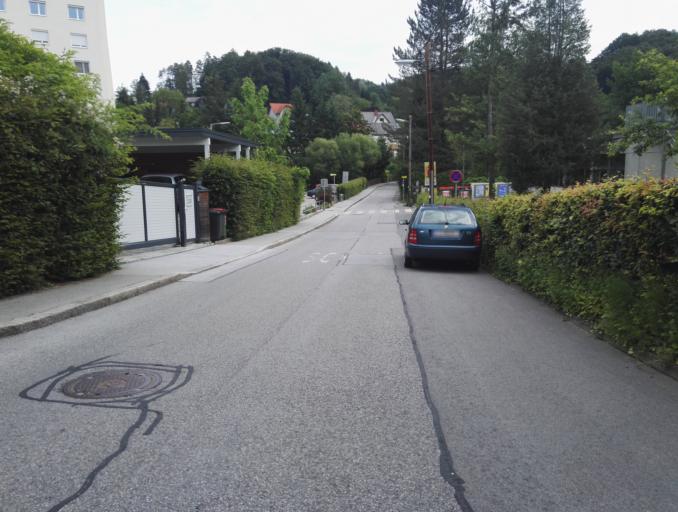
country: AT
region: Styria
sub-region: Graz Stadt
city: Mariatrost
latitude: 47.0747
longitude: 15.4994
